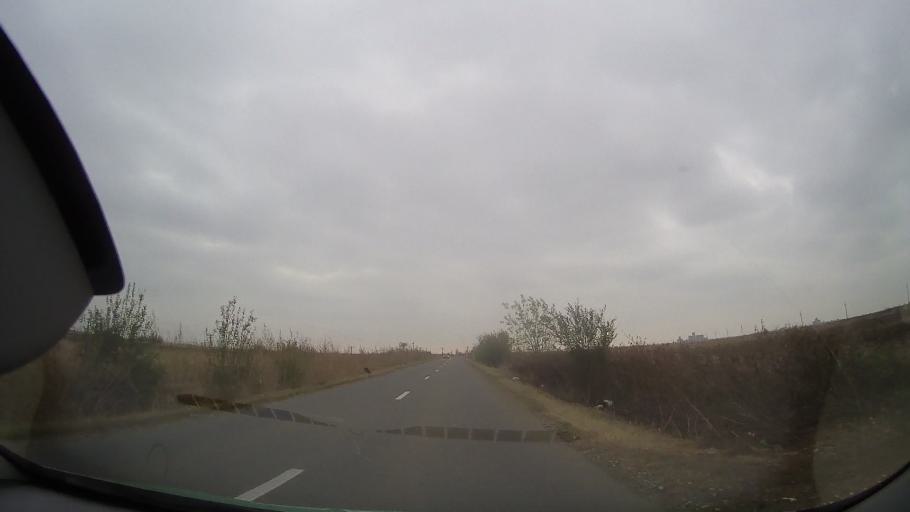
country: RO
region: Ialomita
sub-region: Comuna Manasia
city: Manasia
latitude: 44.7254
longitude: 26.6919
